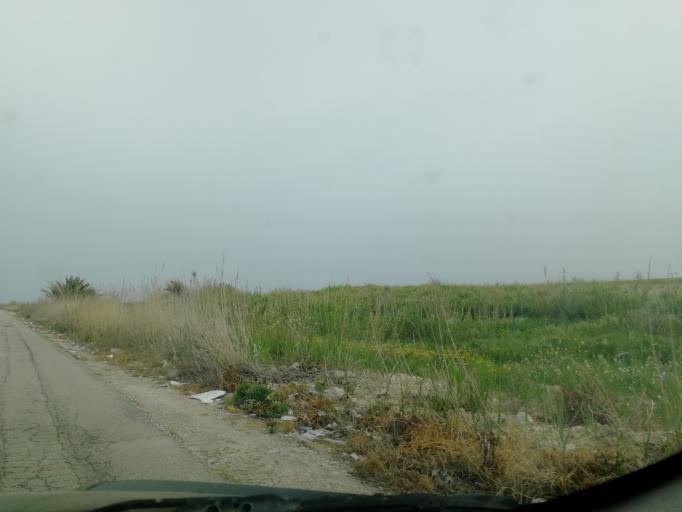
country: IT
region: Apulia
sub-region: Provincia di Barletta - Andria - Trani
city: Barletta
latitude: 41.3178
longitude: 16.3063
